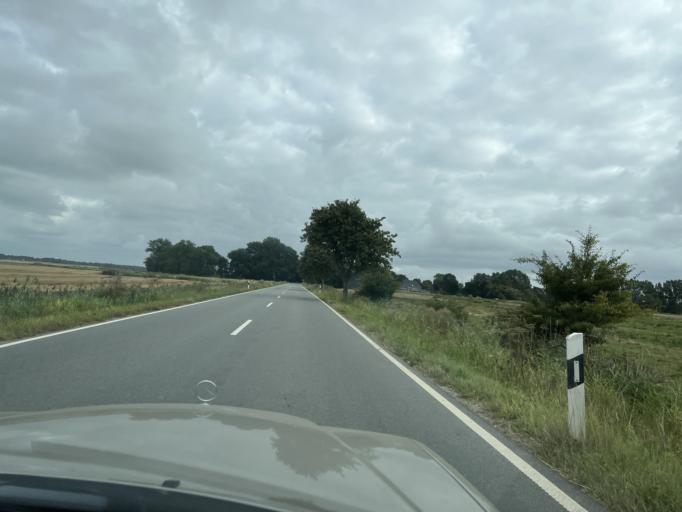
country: DE
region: Schleswig-Holstein
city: Hemme
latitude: 54.2916
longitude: 9.0162
